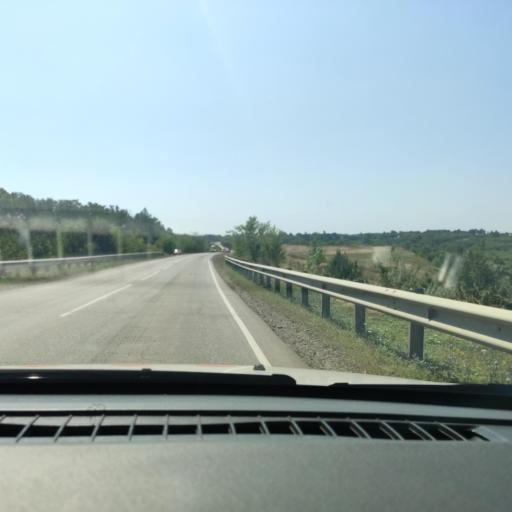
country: RU
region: Voronezj
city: Imeni Pervogo Maya
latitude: 50.7614
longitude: 39.3900
